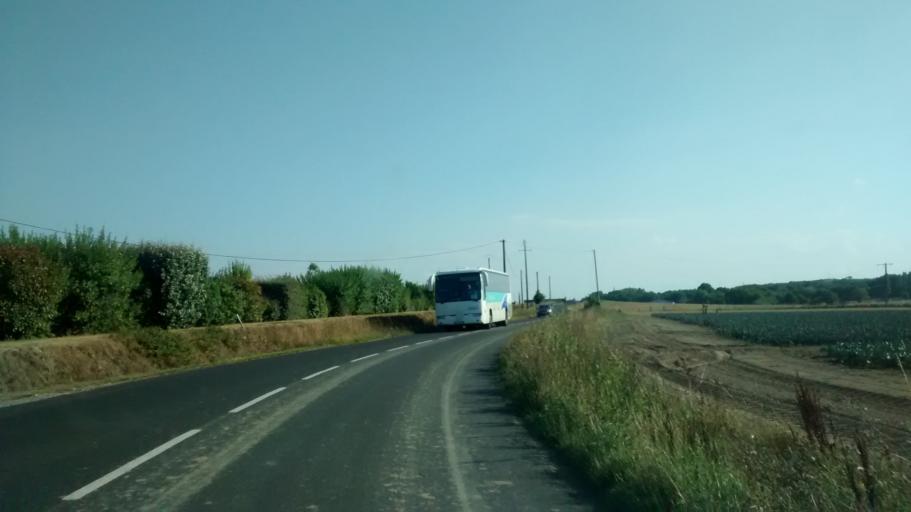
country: FR
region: Brittany
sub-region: Departement d'Ille-et-Vilaine
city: Saint-Coulomb
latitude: 48.6624
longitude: -1.9026
